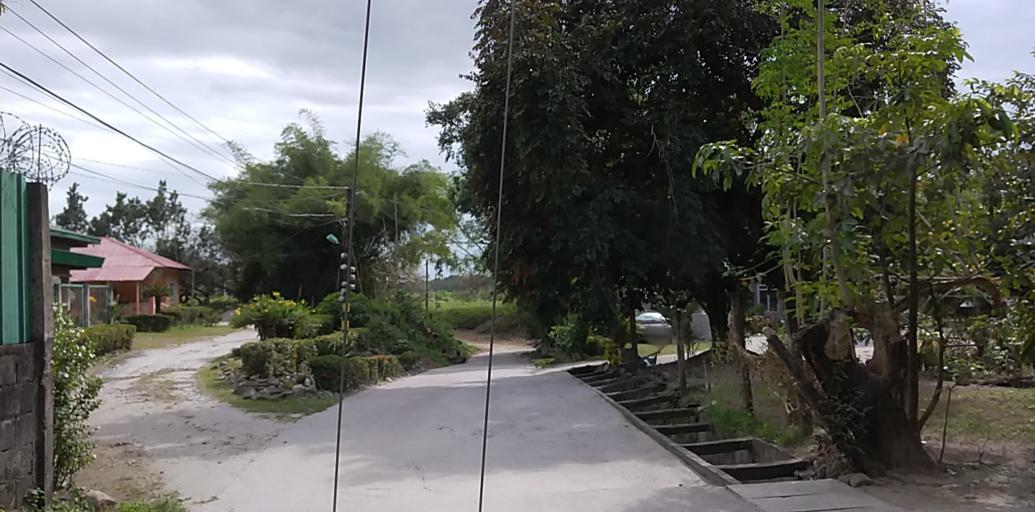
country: PH
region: Central Luzon
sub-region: Province of Pampanga
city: Pulung Santol
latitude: 15.0444
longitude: 120.5555
